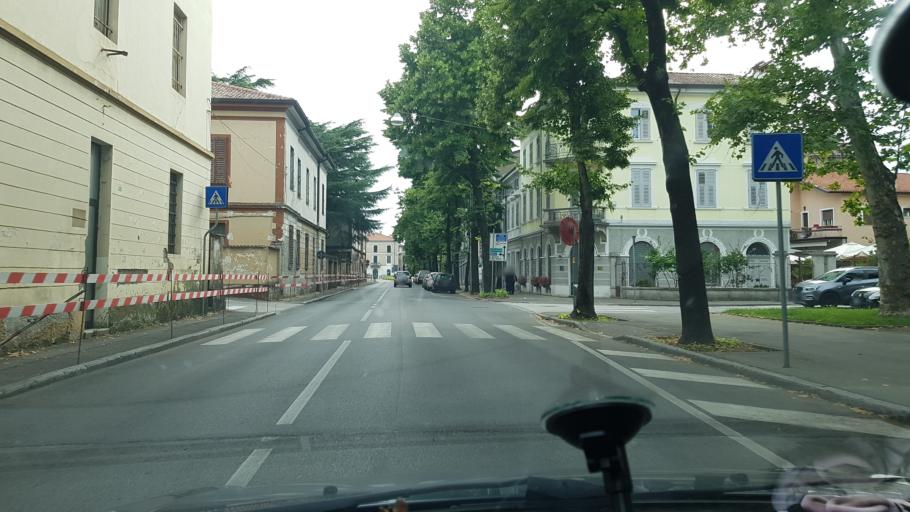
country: IT
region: Friuli Venezia Giulia
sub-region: Provincia di Gorizia
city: Gorizia
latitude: 45.9366
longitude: 13.6153
